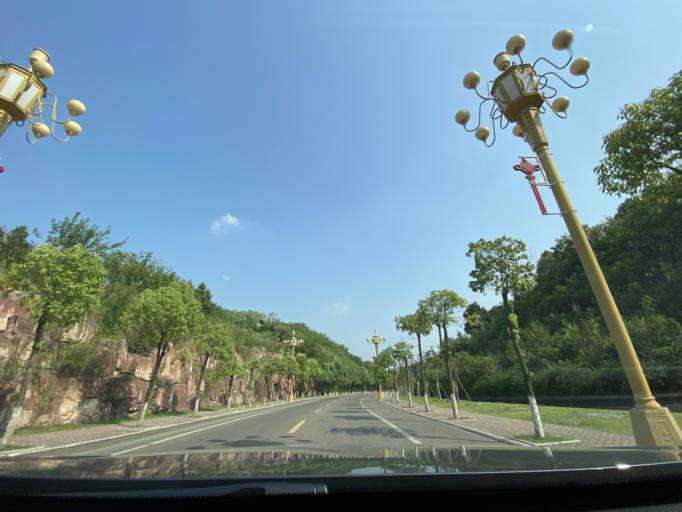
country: CN
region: Sichuan
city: Jiancheng
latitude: 30.4205
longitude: 104.5464
